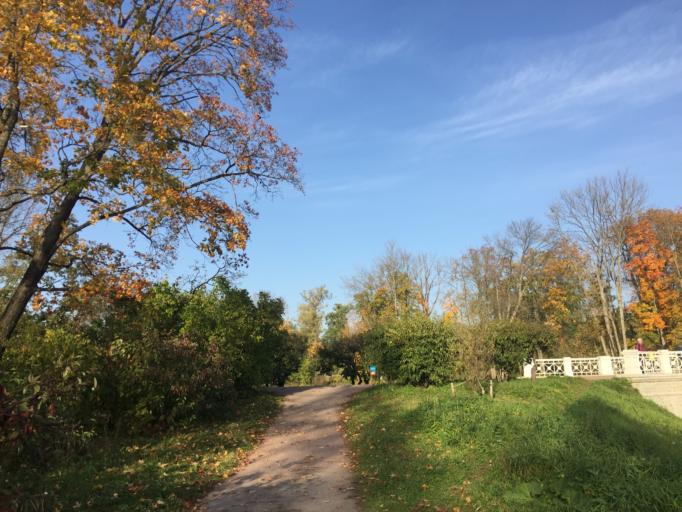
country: RU
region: St.-Petersburg
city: Pushkin
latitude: 59.7223
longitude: 30.3720
